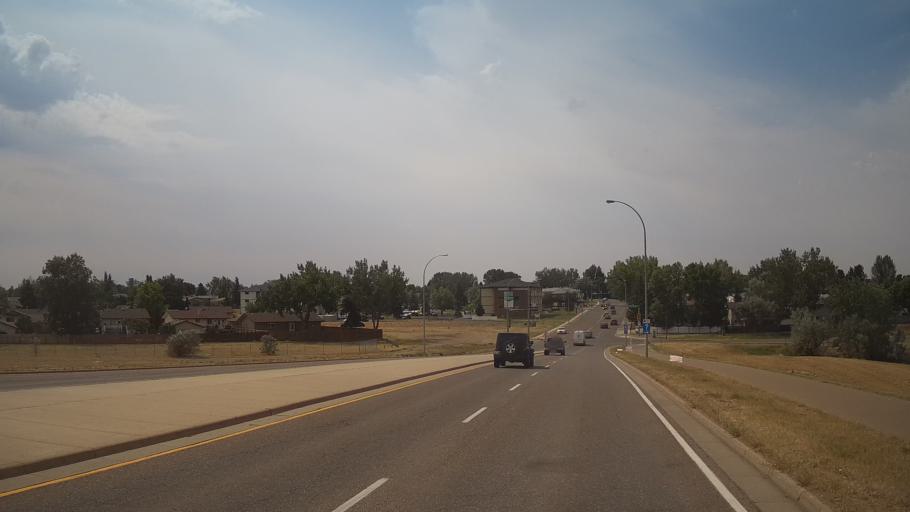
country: CA
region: Alberta
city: Medicine Hat
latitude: 50.0113
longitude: -110.6834
